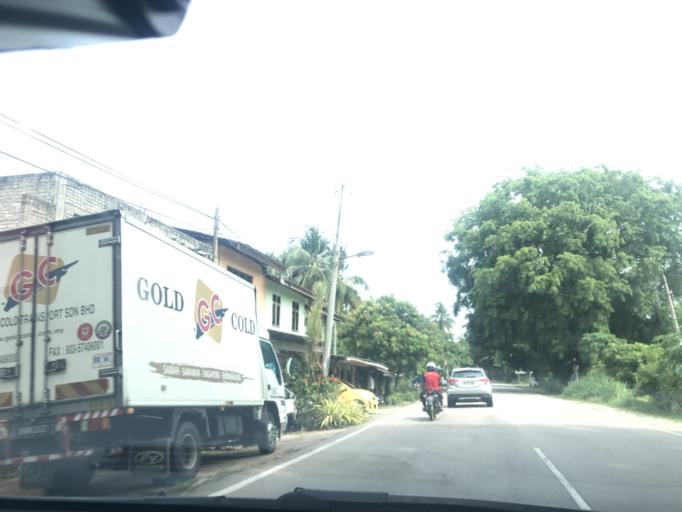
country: MY
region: Kelantan
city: Tumpat
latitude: 6.2127
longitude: 102.1304
